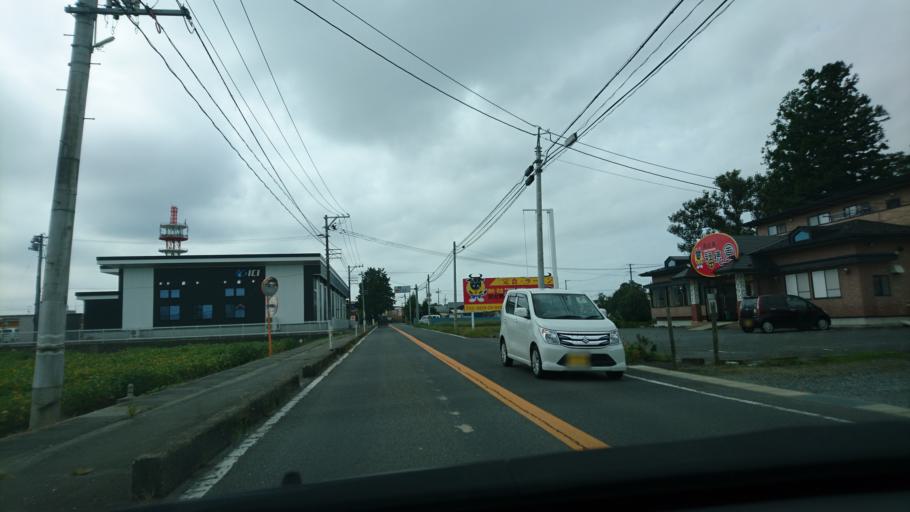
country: JP
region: Miyagi
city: Furukawa
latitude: 38.7378
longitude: 141.0340
